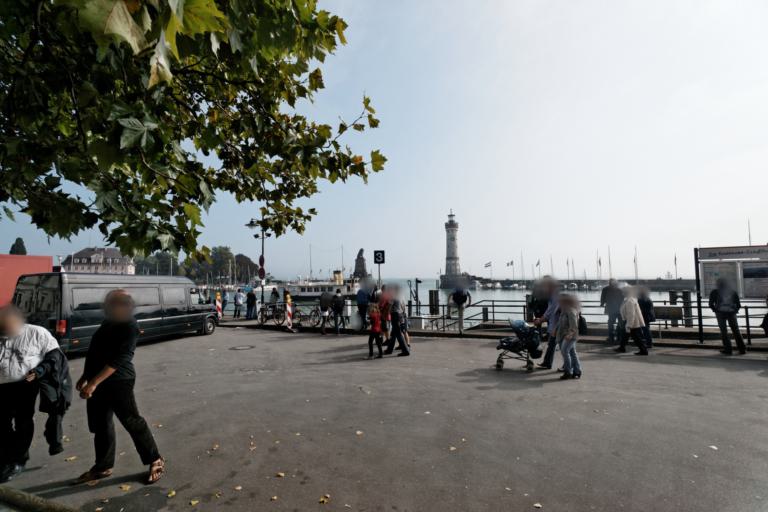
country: DE
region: Bavaria
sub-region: Swabia
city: Lindau
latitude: 47.5439
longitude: 9.6818
